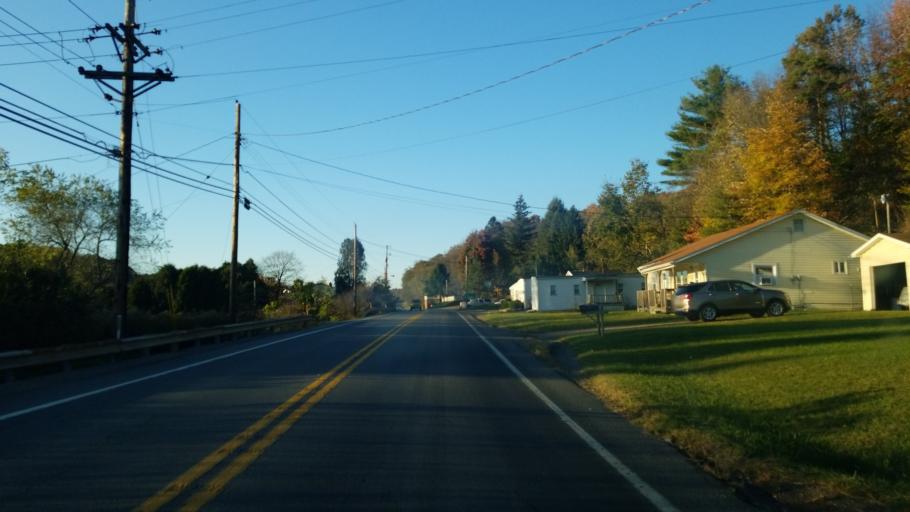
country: US
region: Pennsylvania
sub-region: Jefferson County
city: Punxsutawney
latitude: 40.9565
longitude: -78.9653
